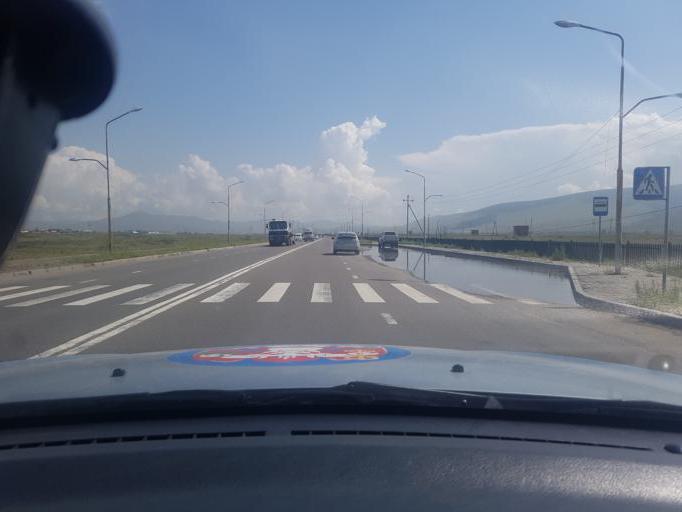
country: MN
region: Ulaanbaatar
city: Ulaanbaatar
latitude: 47.9032
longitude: 106.9800
